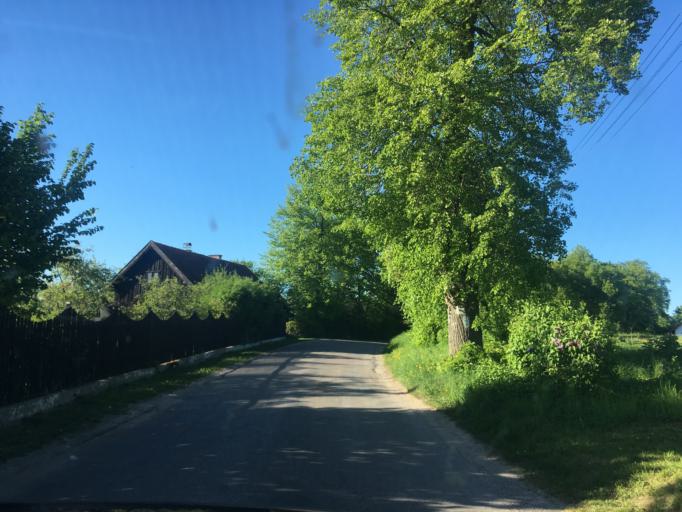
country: PL
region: Warmian-Masurian Voivodeship
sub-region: Powiat piski
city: Ruciane-Nida
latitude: 53.6676
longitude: 21.4813
